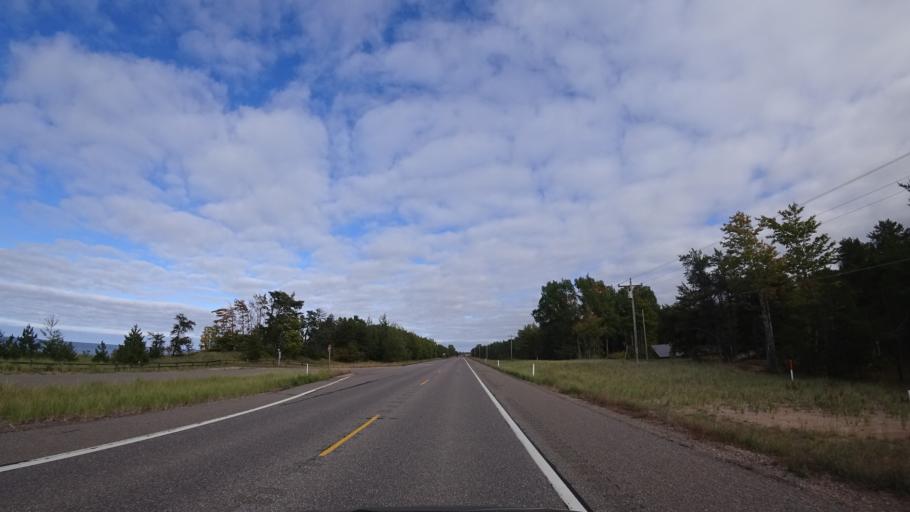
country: US
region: Michigan
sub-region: Marquette County
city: Harvey
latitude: 46.4897
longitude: -87.2070
